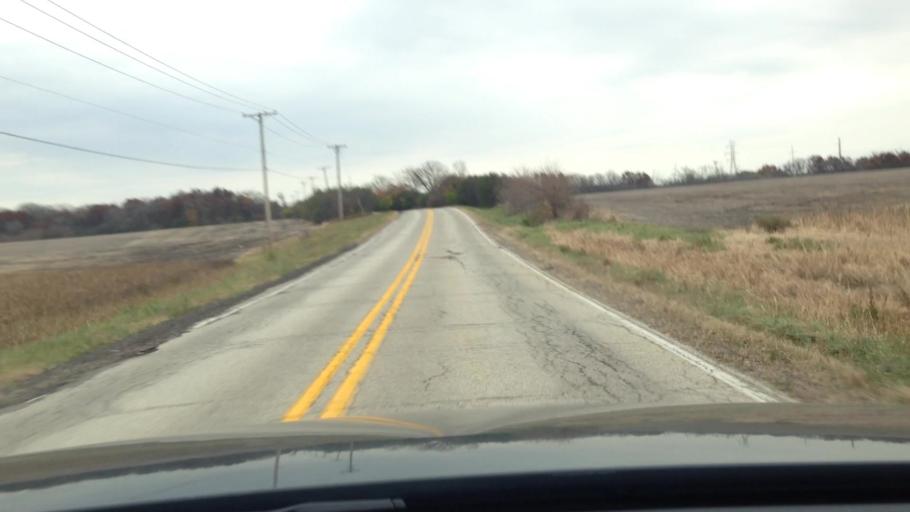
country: US
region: Illinois
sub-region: McHenry County
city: Woodstock
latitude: 42.2723
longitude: -88.4432
